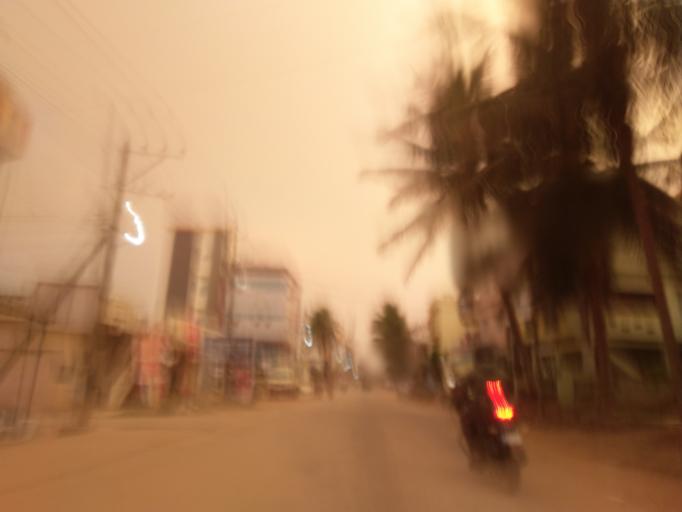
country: IN
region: Karnataka
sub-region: Hassan
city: Hassan
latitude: 13.0191
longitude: 76.1135
